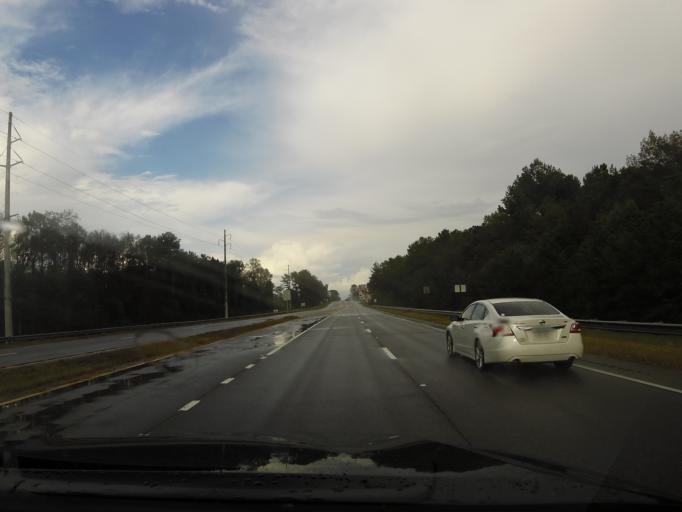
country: US
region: Georgia
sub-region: Long County
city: Ludowici
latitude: 31.7069
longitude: -81.7576
